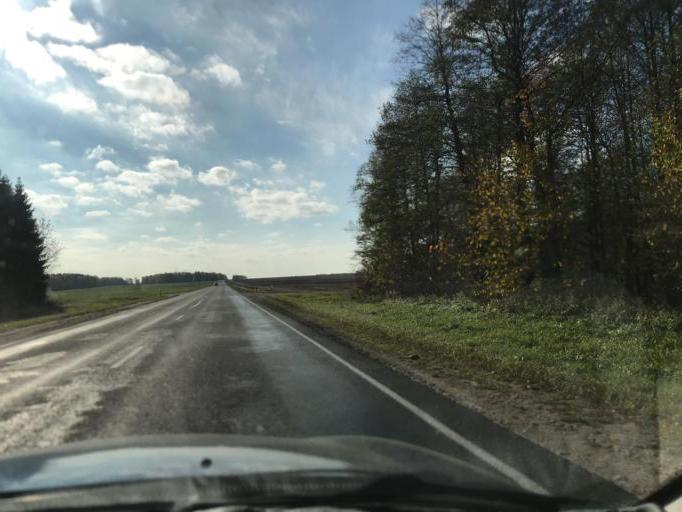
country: BY
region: Grodnenskaya
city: Voranava
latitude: 54.2019
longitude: 25.3482
